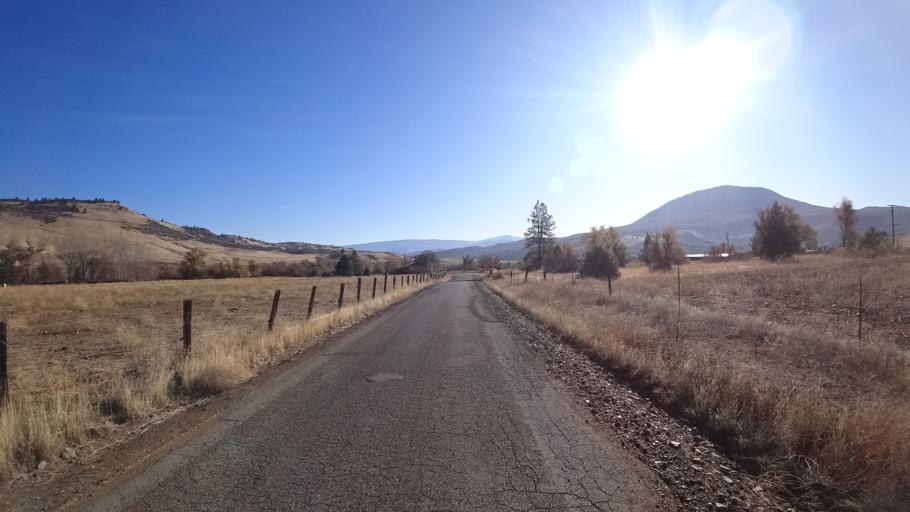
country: US
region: California
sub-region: Siskiyou County
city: Montague
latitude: 41.8996
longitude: -122.5534
